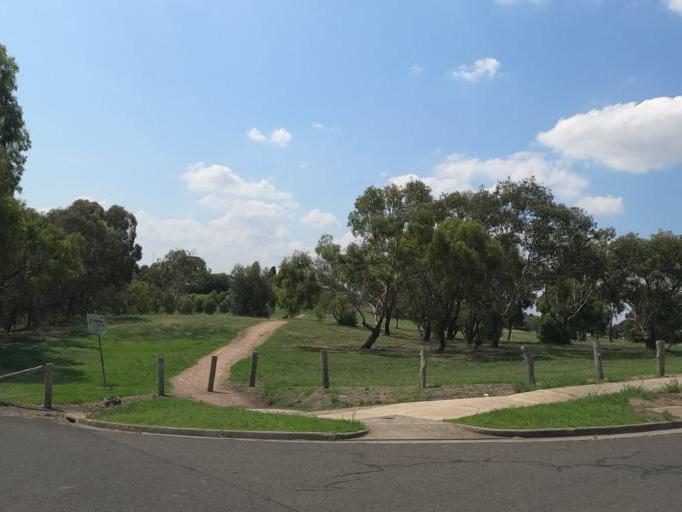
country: AU
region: Victoria
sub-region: Hume
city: Broadmeadows
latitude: -37.6722
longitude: 144.9182
